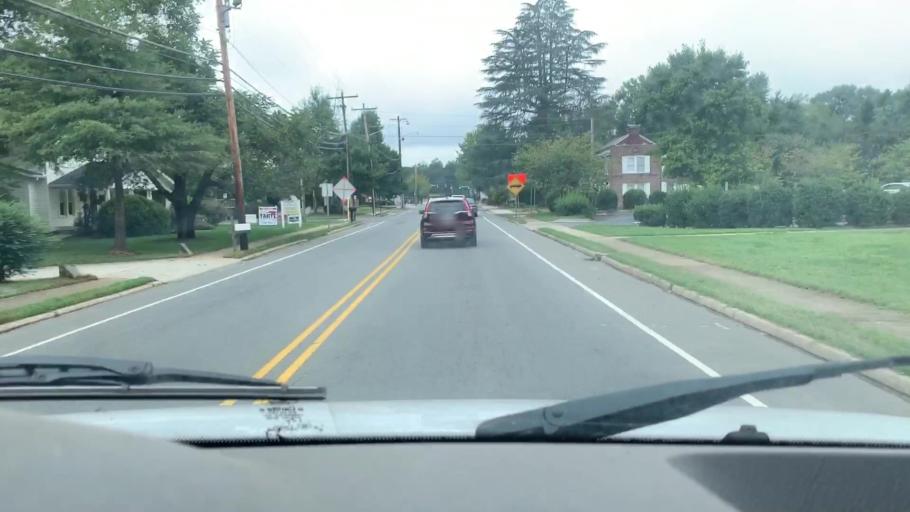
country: US
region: North Carolina
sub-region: Mecklenburg County
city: Huntersville
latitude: 35.4083
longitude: -80.8423
